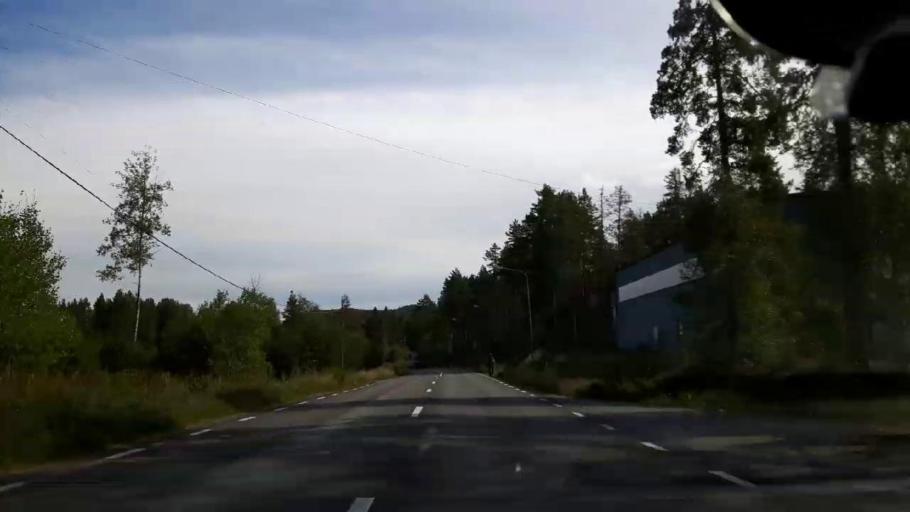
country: SE
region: Jaemtland
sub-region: Braecke Kommun
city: Braecke
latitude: 63.1622
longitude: 15.5727
